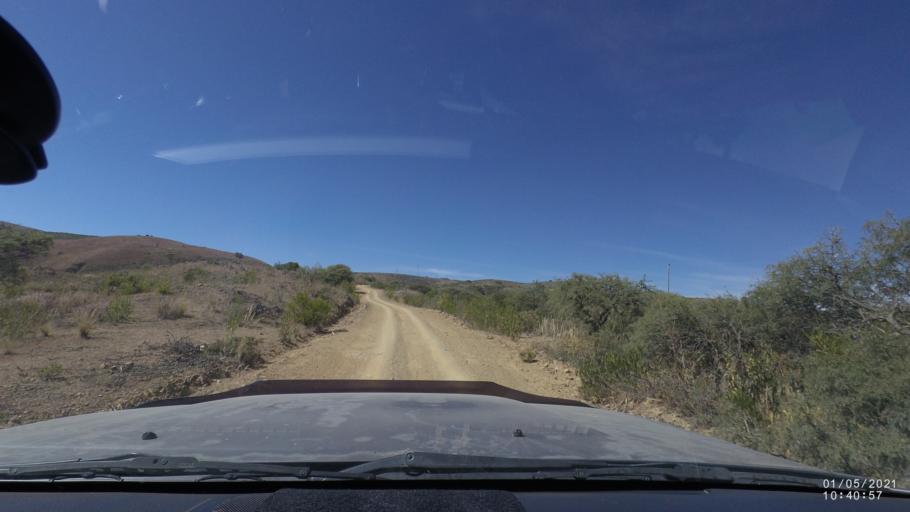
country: BO
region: Cochabamba
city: Capinota
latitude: -17.6064
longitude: -66.1794
